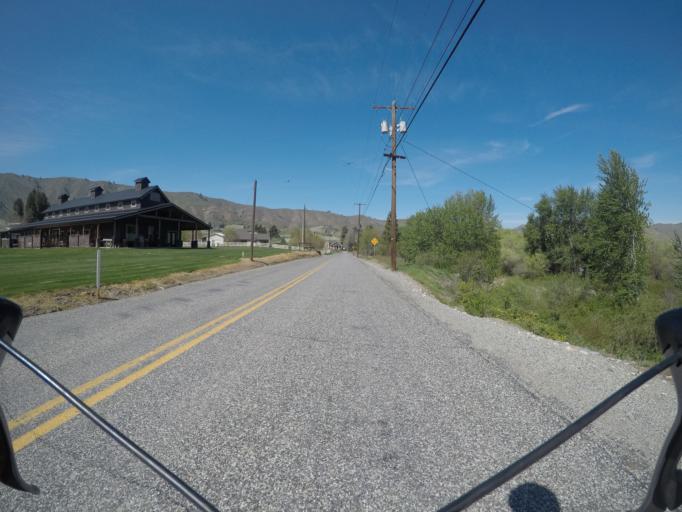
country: US
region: Washington
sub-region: Chelan County
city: Cashmere
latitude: 47.4904
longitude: -120.4236
